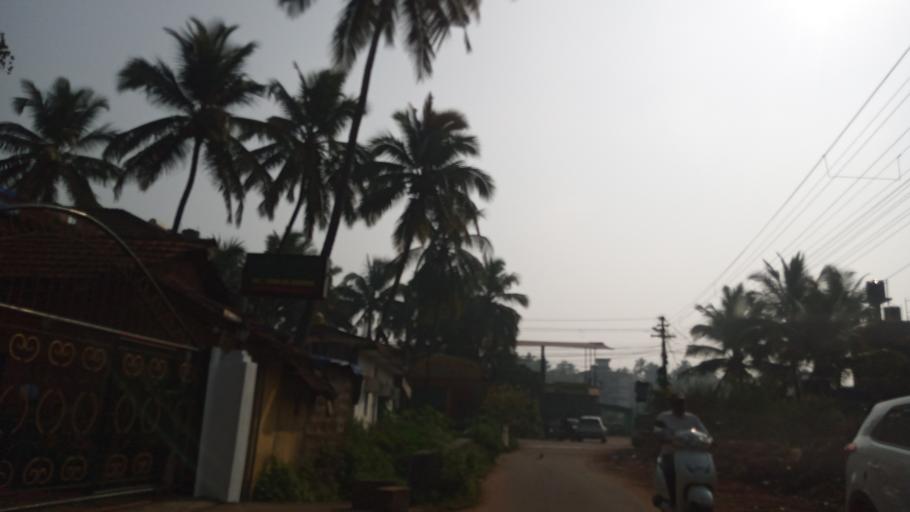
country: IN
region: Goa
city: Calangute
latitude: 15.5415
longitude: 73.7605
